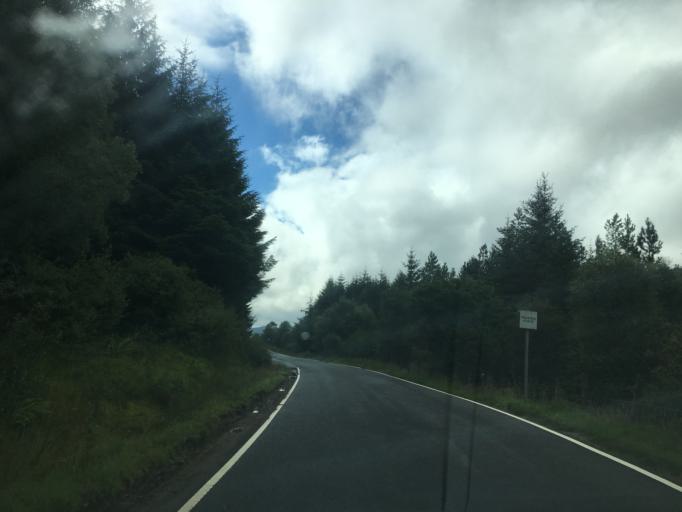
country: GB
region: Scotland
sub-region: Argyll and Bute
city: Port Bannatyne
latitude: 56.0072
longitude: -5.0807
